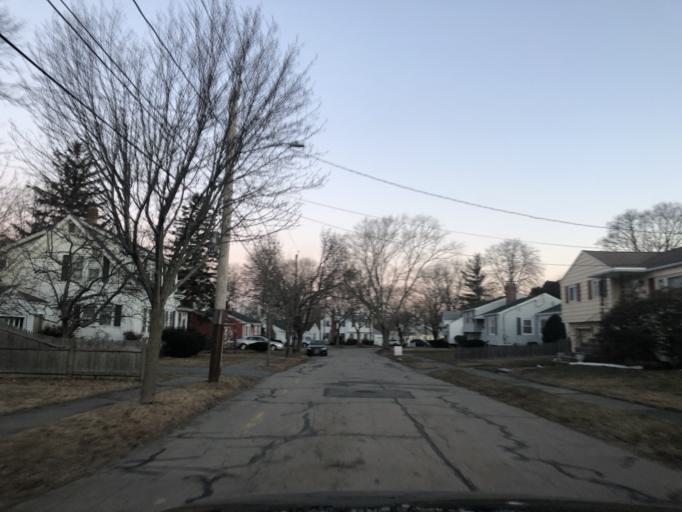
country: US
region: Massachusetts
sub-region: Norfolk County
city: Milton
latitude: 42.2650
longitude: -71.0452
